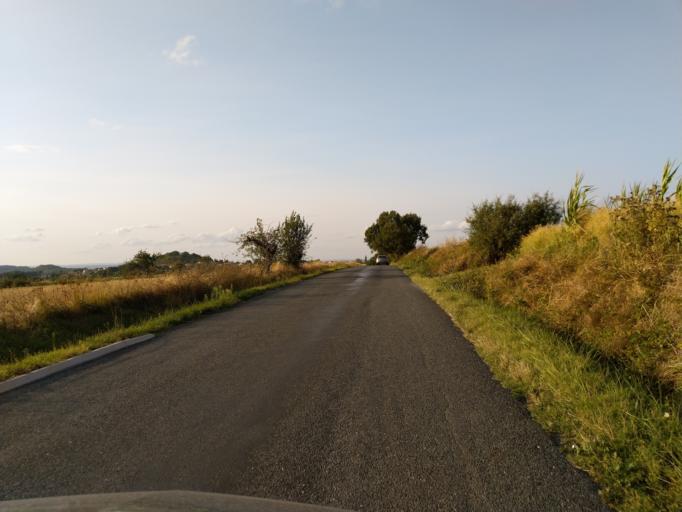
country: FR
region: Midi-Pyrenees
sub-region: Departement du Tarn
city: Frejairolles
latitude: 43.8687
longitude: 2.2336
